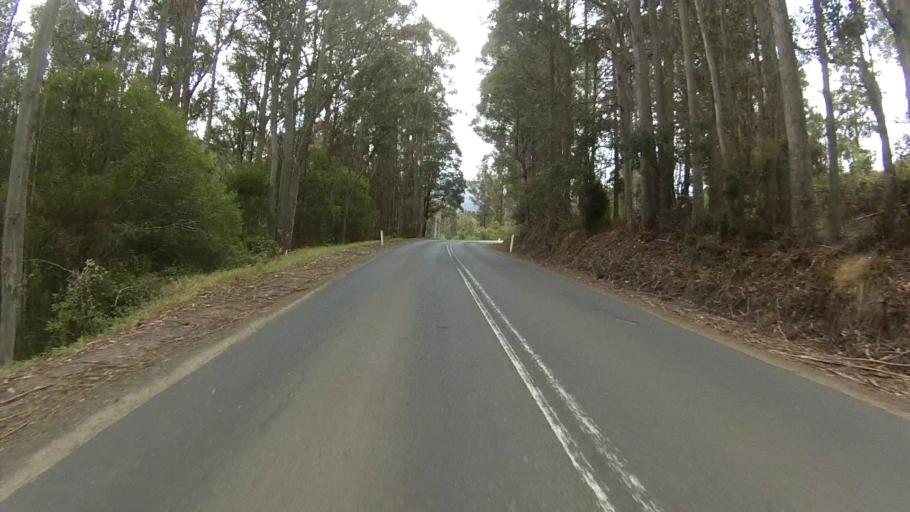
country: AU
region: Tasmania
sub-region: Huon Valley
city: Cygnet
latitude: -43.1387
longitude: 147.1518
